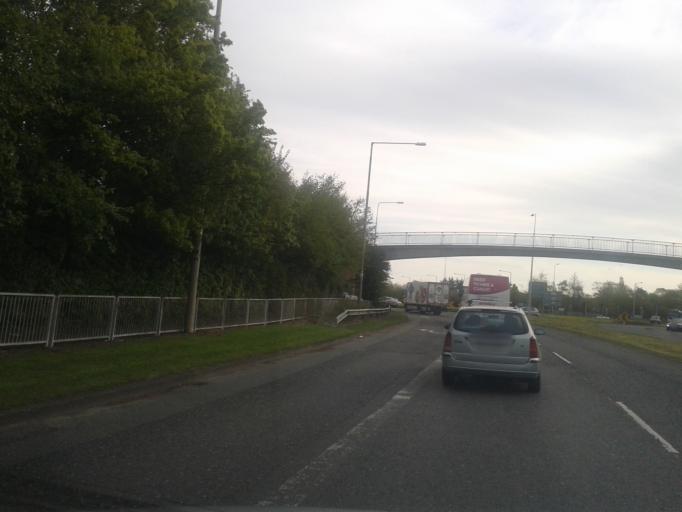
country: IE
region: Leinster
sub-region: Fingal County
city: Swords
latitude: 53.4533
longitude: -6.2156
